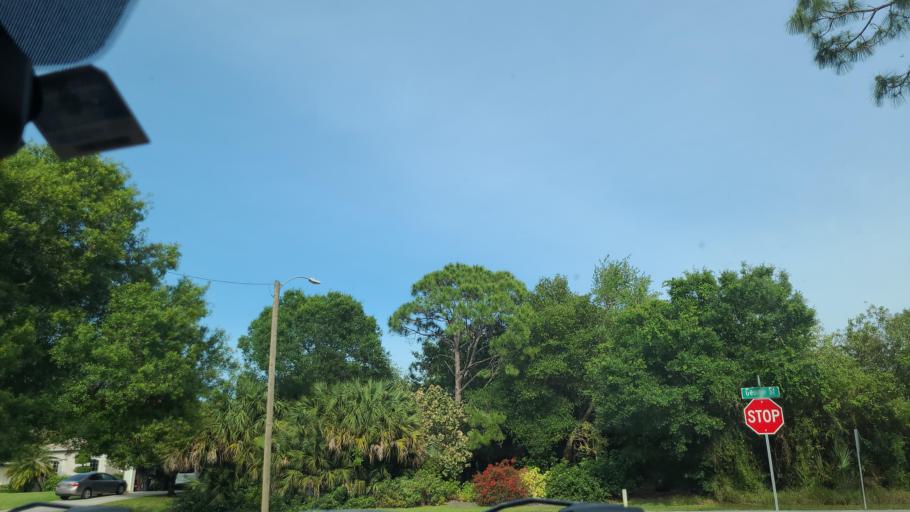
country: US
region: Florida
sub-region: Indian River County
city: Sebastian
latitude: 27.7729
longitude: -80.4793
